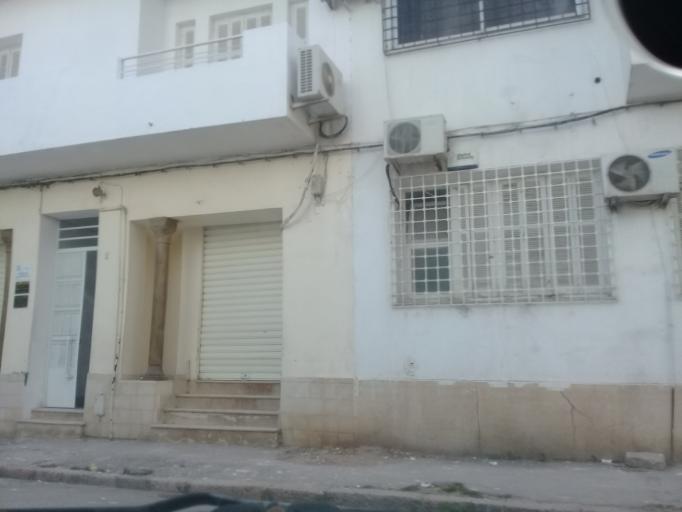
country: TN
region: Tunis
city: Tunis
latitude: 36.8192
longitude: 10.1801
